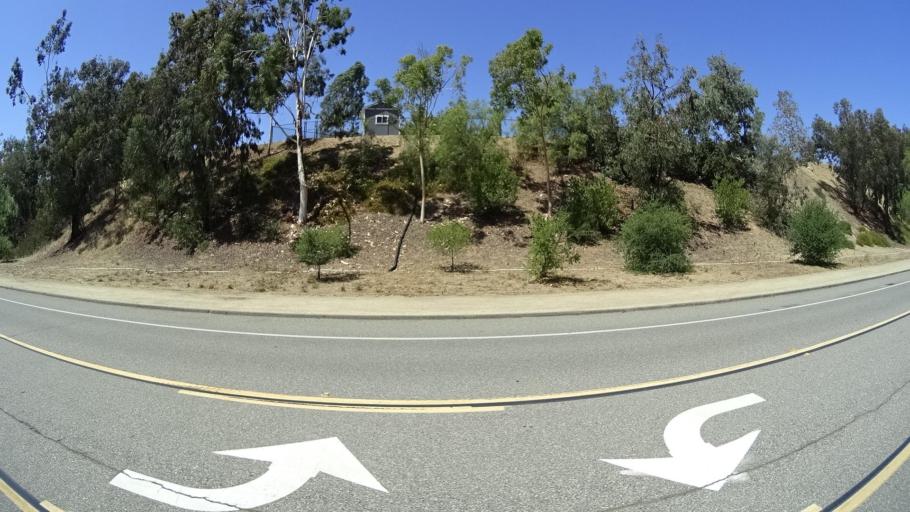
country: US
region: California
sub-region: San Diego County
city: Bonsall
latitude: 33.3273
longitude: -117.1924
